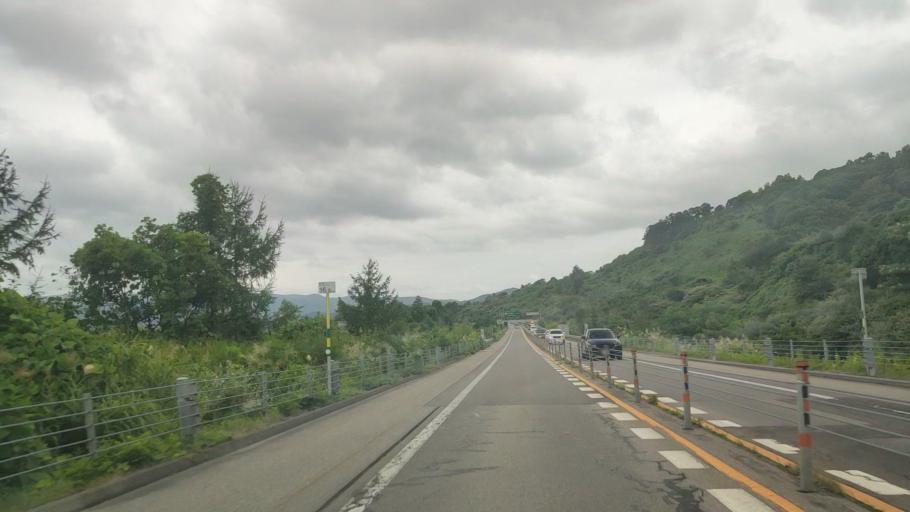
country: JP
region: Hokkaido
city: Nanae
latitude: 41.9110
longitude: 140.6932
